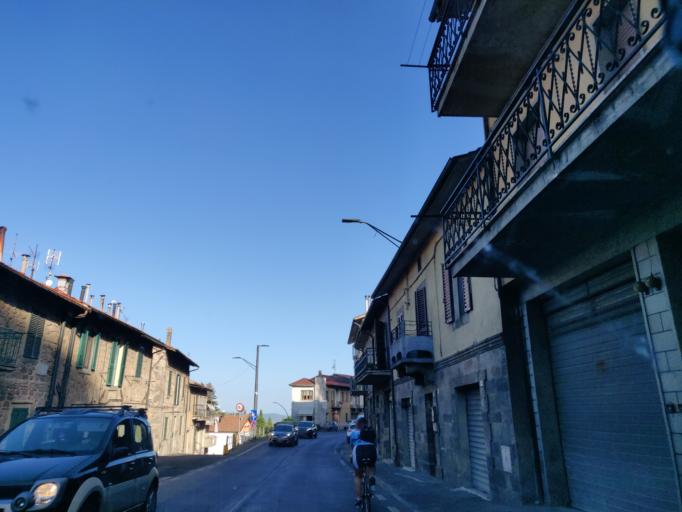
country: IT
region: Tuscany
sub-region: Provincia di Siena
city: Abbadia San Salvatore
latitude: 42.8772
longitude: 11.6819
